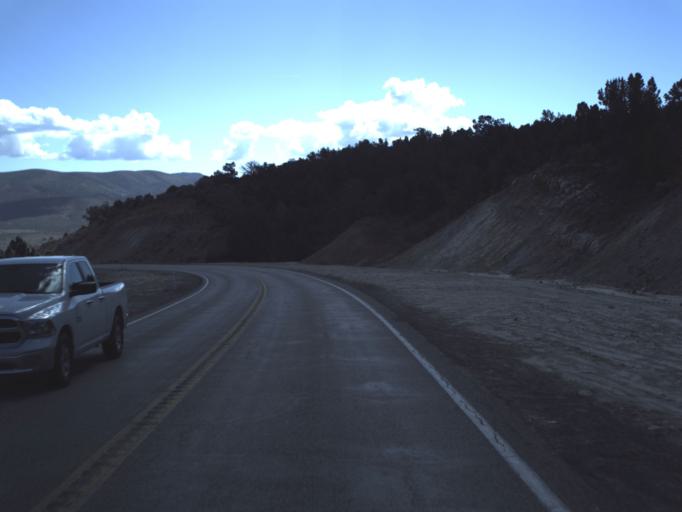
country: US
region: Utah
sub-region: Washington County
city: Enterprise
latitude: 37.5273
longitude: -113.6466
